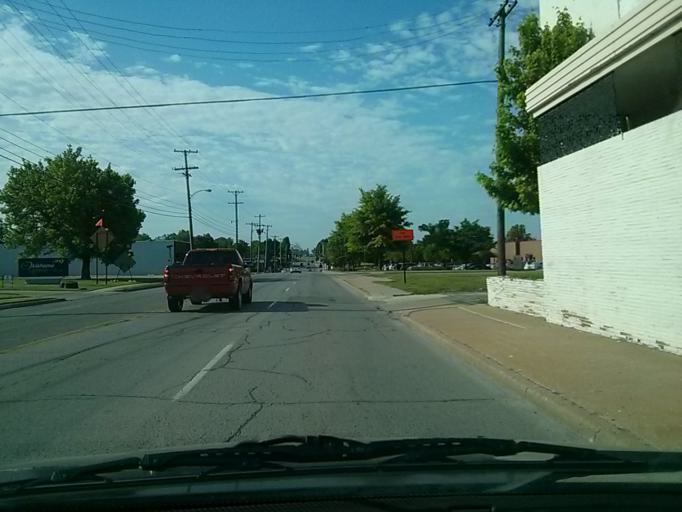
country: US
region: Oklahoma
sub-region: Tulsa County
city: Tulsa
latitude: 36.1544
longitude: -95.9757
